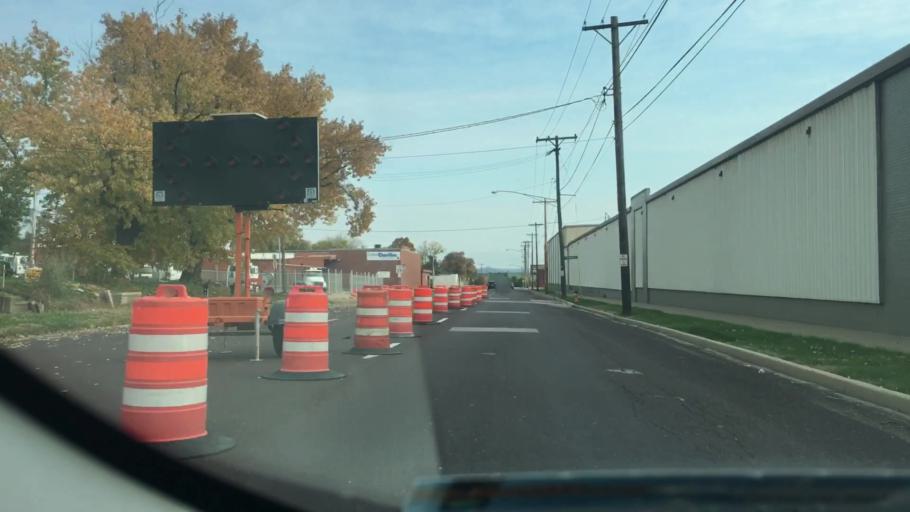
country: US
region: Illinois
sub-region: Peoria County
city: North Peoria
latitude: 40.7043
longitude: -89.5698
